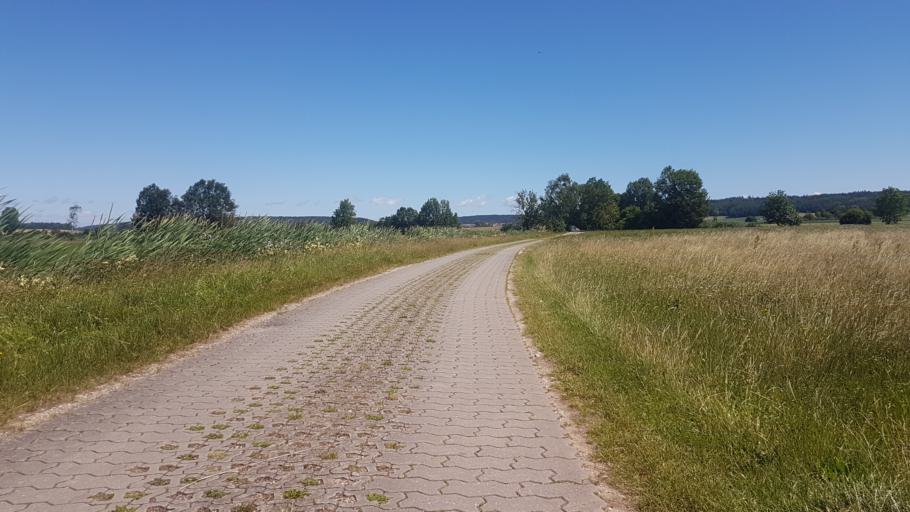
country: DE
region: Bavaria
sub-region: Regierungsbezirk Mittelfranken
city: Herrieden
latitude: 49.2136
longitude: 10.5292
